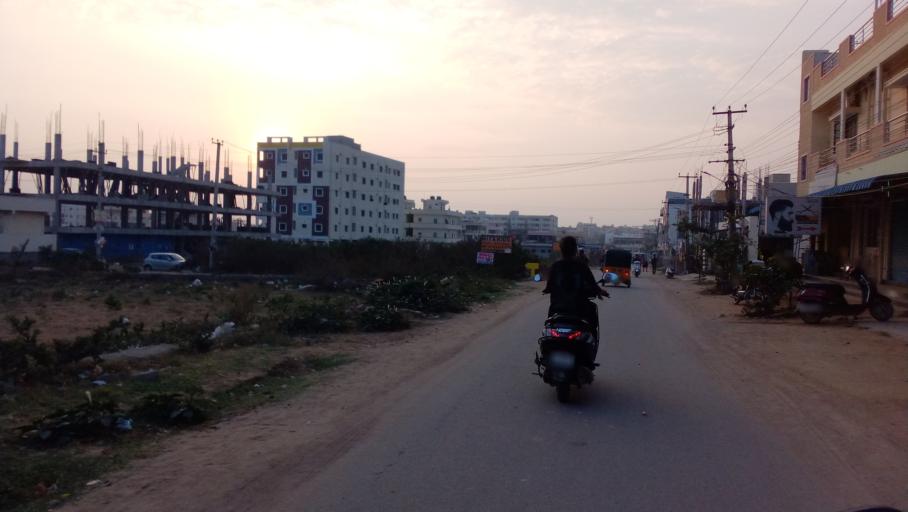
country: IN
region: Telangana
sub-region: Medak
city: Serilingampalle
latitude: 17.5177
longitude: 78.3181
